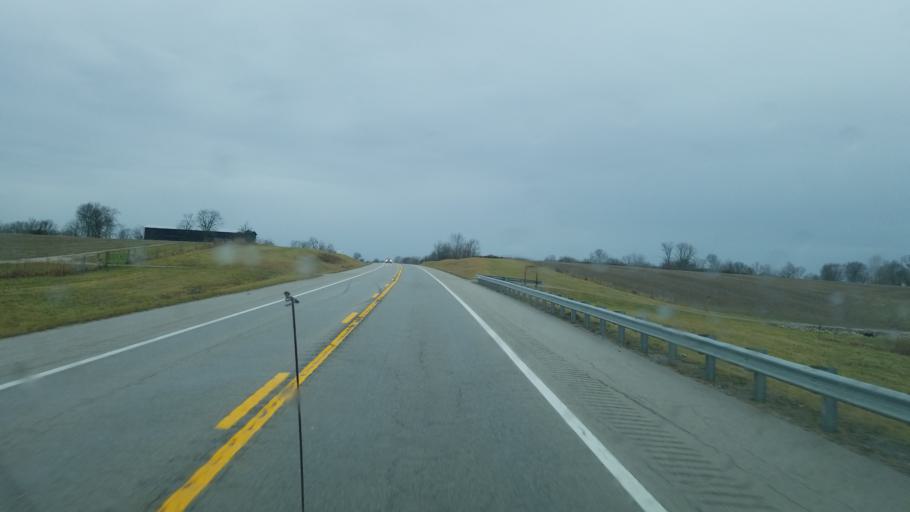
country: US
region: Ohio
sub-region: Adams County
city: Manchester
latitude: 38.5649
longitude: -83.6249
